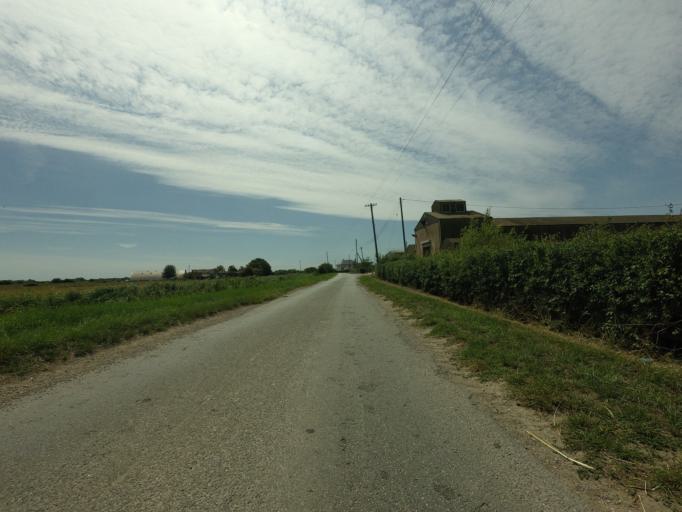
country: GB
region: England
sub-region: Kent
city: Stone
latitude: 51.0158
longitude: 0.7942
